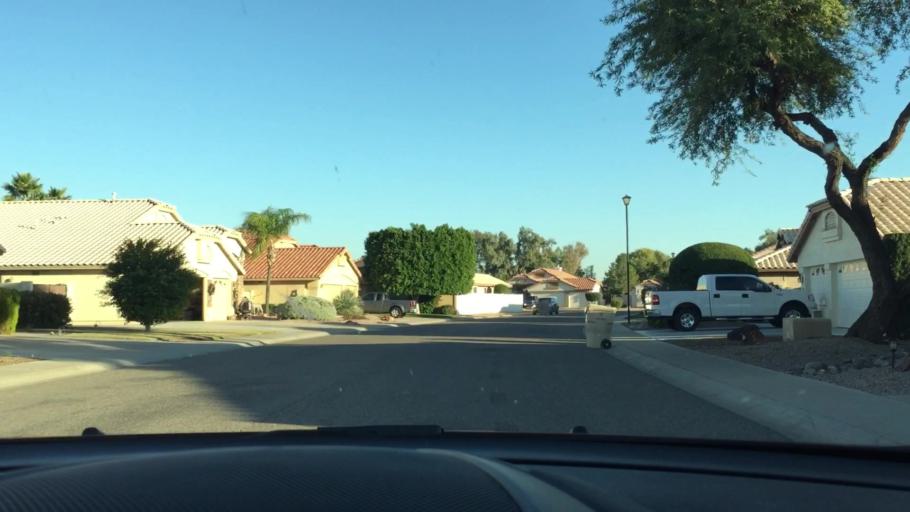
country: US
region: Arizona
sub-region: Maricopa County
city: Sun City
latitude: 33.6627
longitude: -112.2276
